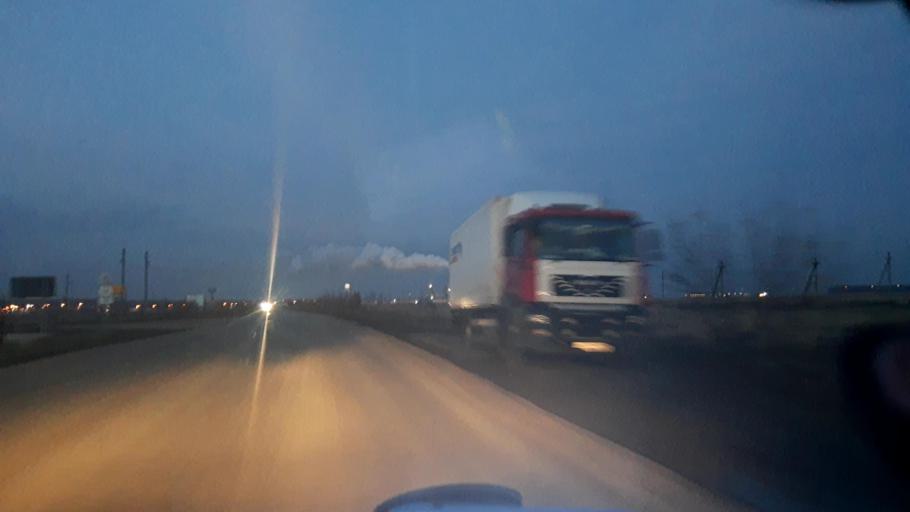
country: RU
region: Bashkortostan
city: Iglino
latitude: 54.7578
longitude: 56.2580
